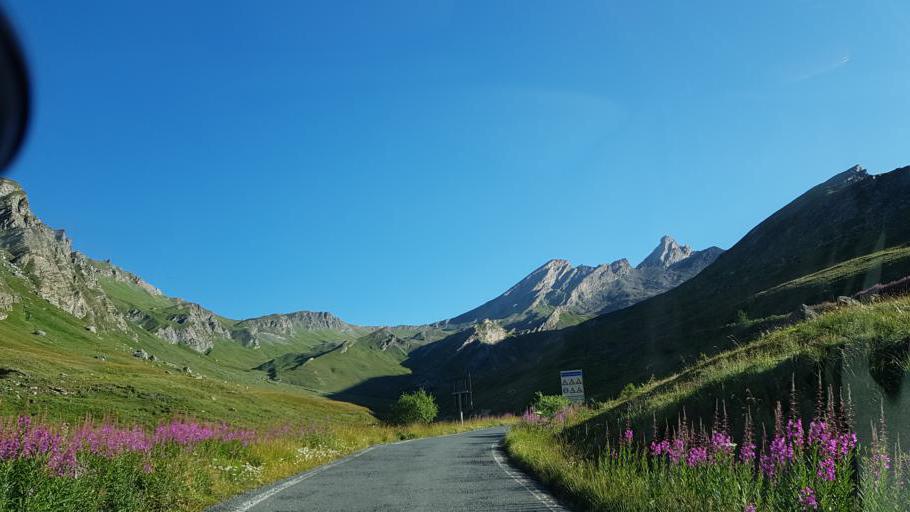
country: IT
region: Piedmont
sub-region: Provincia di Cuneo
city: Pontechianale
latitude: 44.6613
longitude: 6.9858
